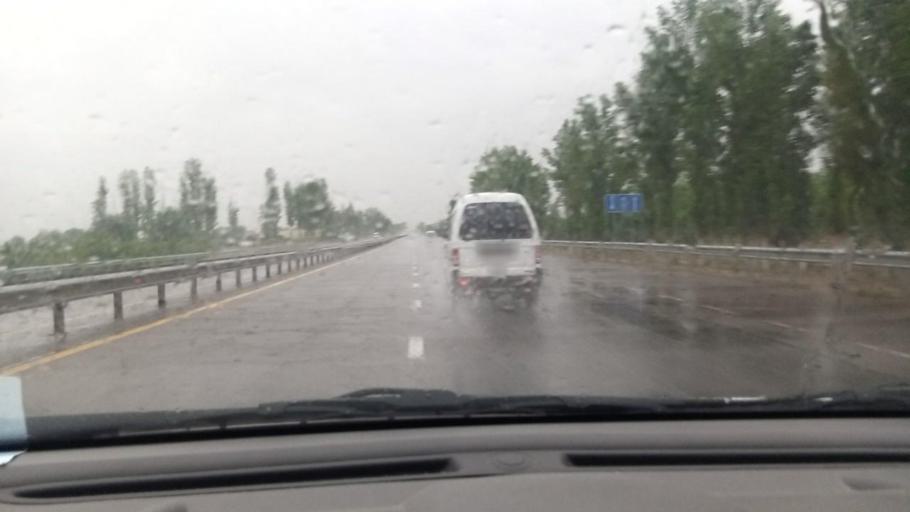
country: UZ
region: Toshkent
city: Tuytepa
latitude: 41.1190
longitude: 69.4429
